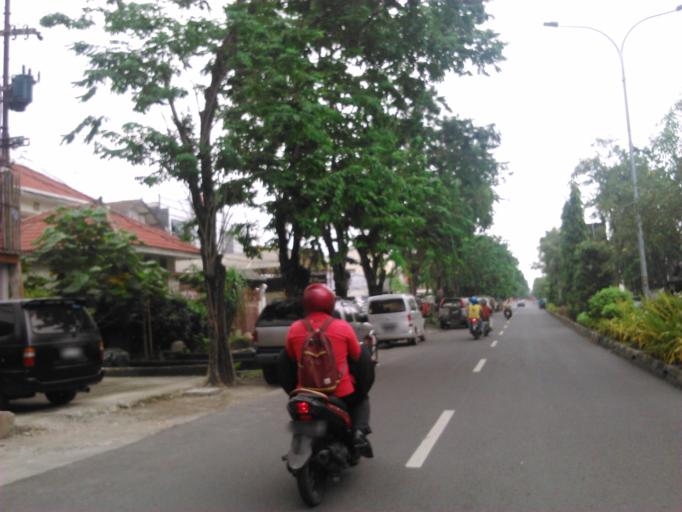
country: ID
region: East Java
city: Gubengairlangga
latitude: -7.2786
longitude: 112.7623
